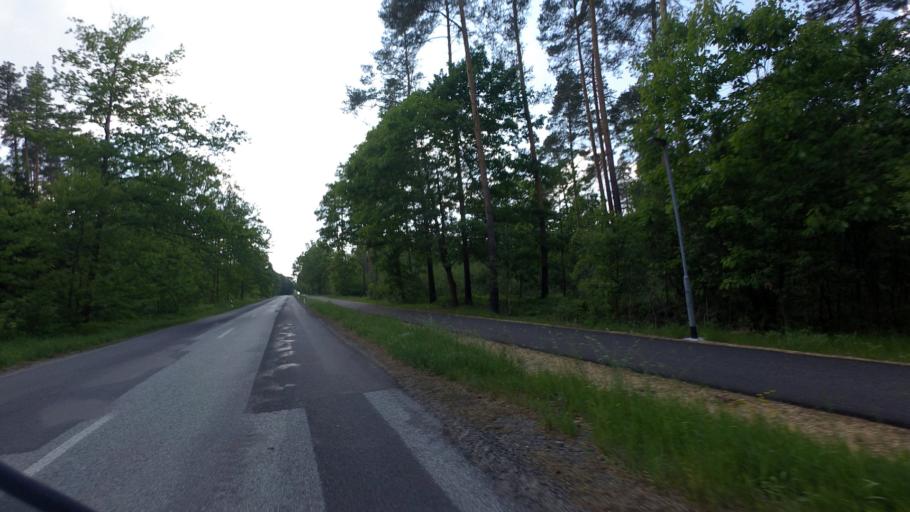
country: DE
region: Saxony
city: Mucka
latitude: 51.3056
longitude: 14.6781
